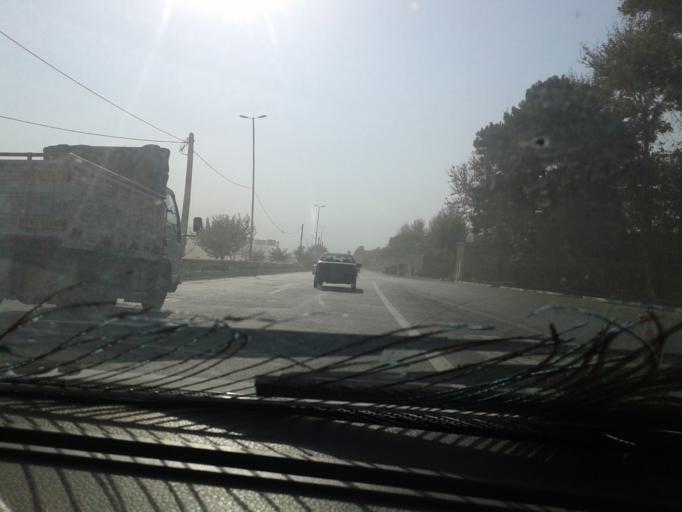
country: IR
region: Tehran
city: Tehran
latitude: 35.7241
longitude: 51.5970
